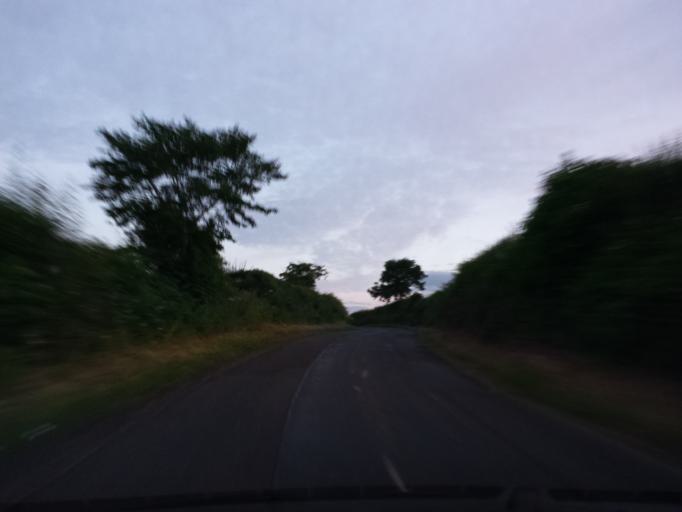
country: GB
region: Scotland
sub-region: The Scottish Borders
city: Chirnside
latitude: 55.8510
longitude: -2.2337
